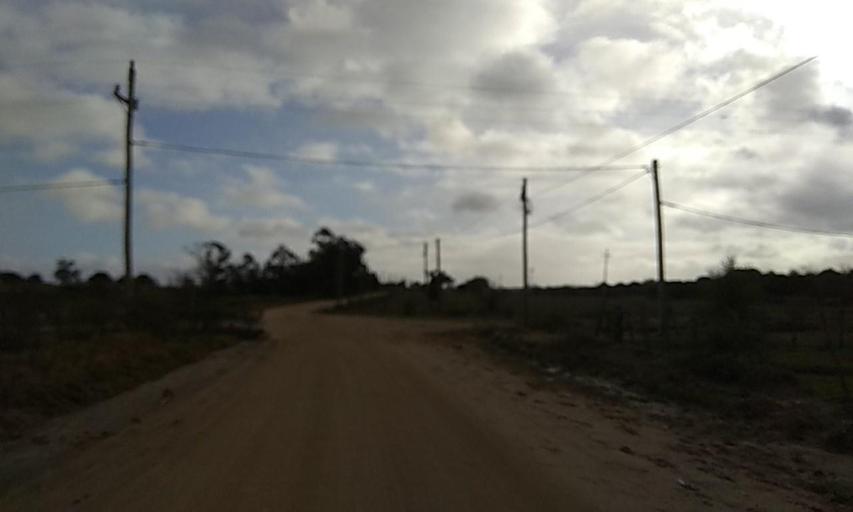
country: UY
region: Florida
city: Florida
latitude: -34.0640
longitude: -56.1932
